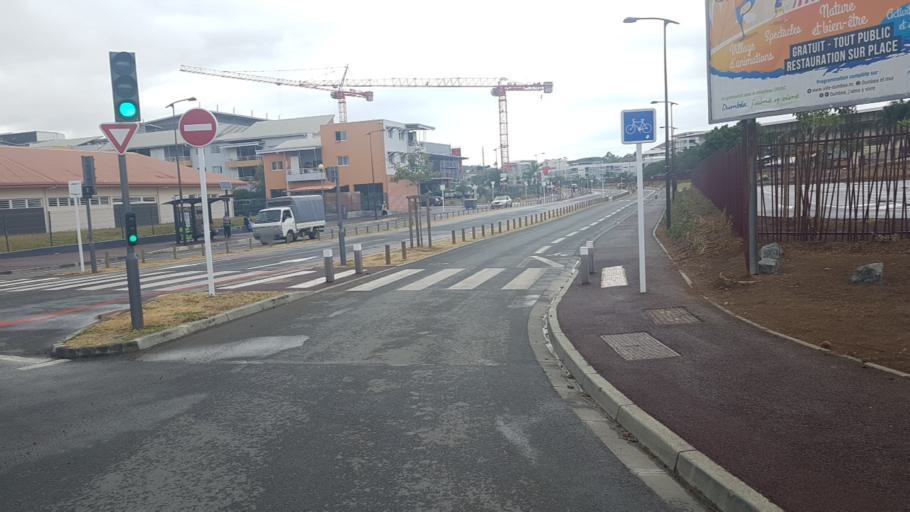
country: NC
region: South Province
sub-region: Noumea
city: Noumea
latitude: -22.2167
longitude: 166.4719
